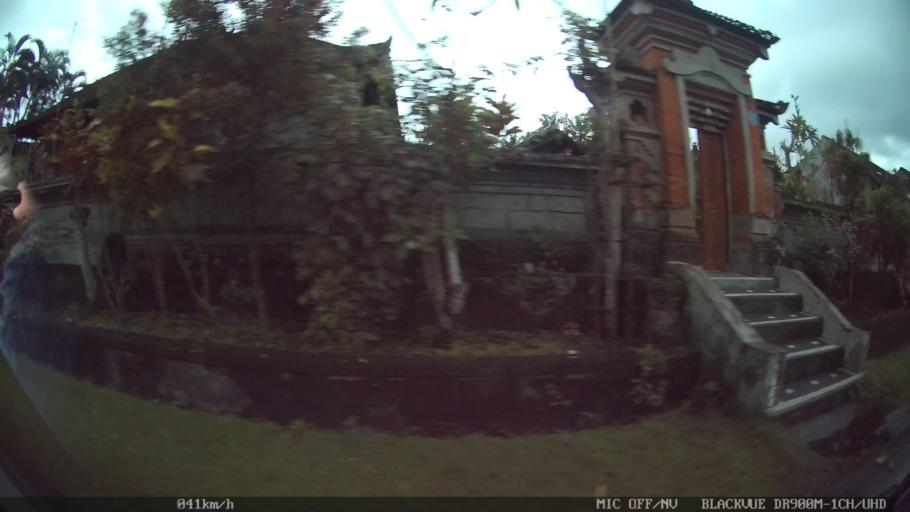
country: ID
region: Bali
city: Banjar Tebongkang
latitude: -8.5240
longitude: 115.2373
